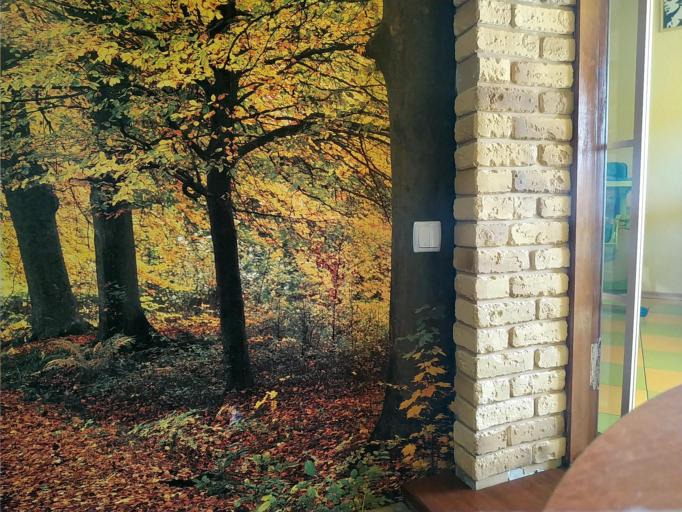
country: RU
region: Smolensk
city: Katyn'
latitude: 54.9898
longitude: 31.7403
